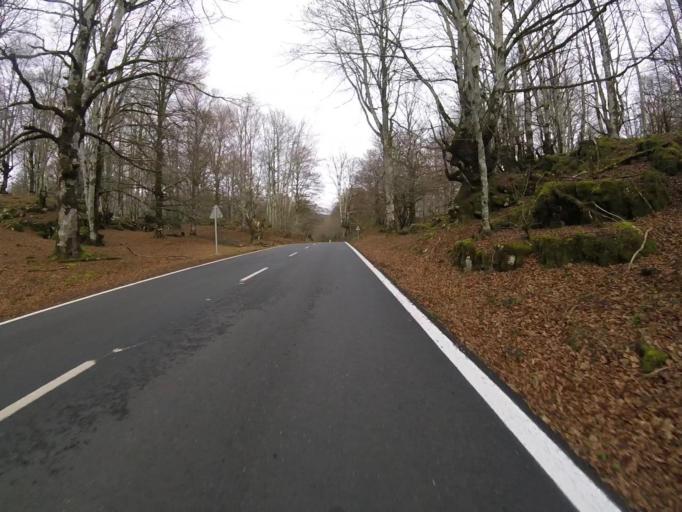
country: ES
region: Navarre
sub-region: Provincia de Navarra
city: Olazagutia
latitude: 42.8425
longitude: -2.1803
